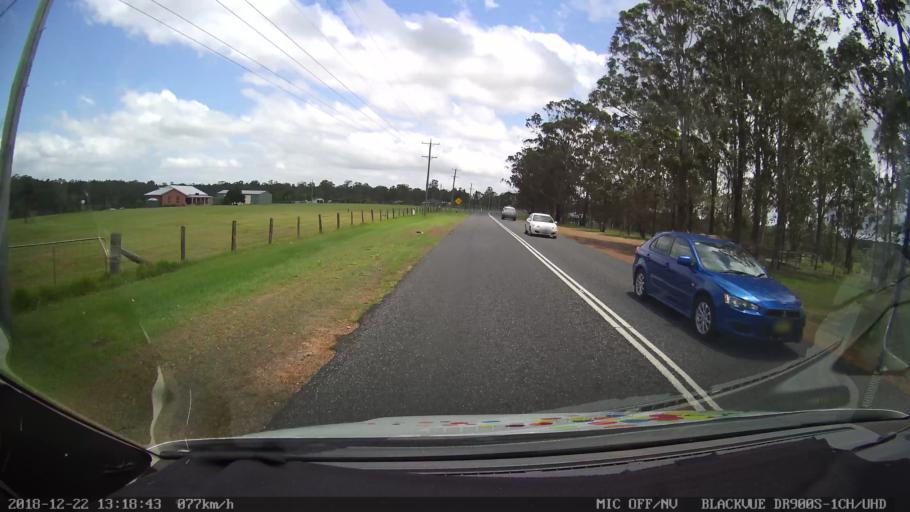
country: AU
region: New South Wales
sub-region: Clarence Valley
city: South Grafton
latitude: -29.7496
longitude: 152.9329
